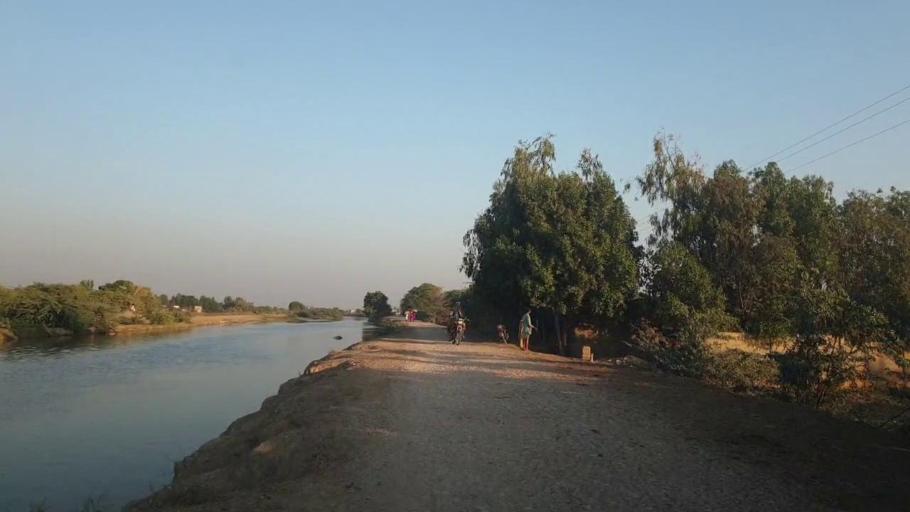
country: PK
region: Sindh
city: Mirpur Sakro
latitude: 24.4618
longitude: 67.5910
